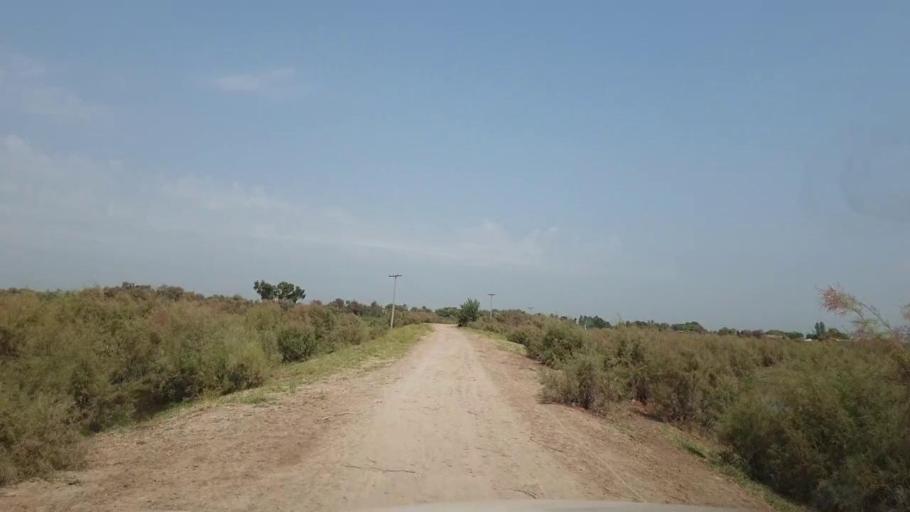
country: PK
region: Sindh
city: Ratodero
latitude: 27.8398
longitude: 68.2485
